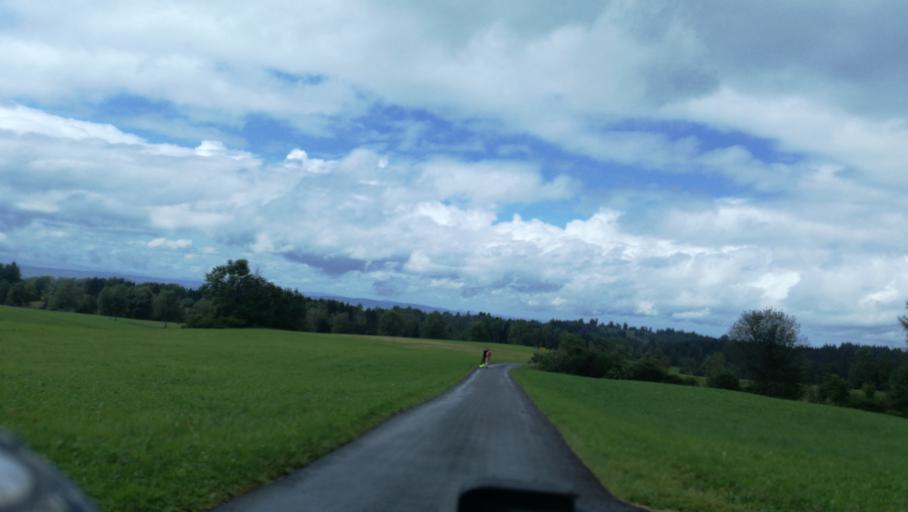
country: CH
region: Zug
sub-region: Zug
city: Walchwil
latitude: 47.1135
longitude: 8.5423
